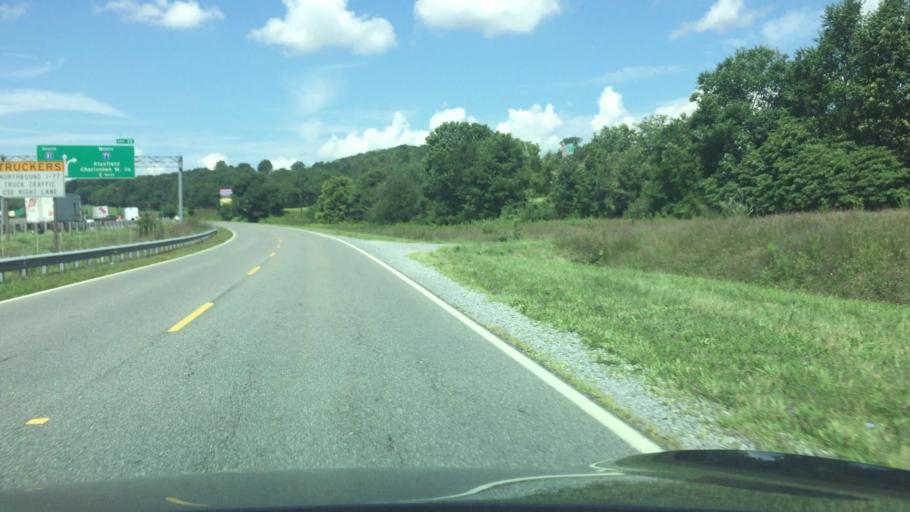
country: US
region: Virginia
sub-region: Wythe County
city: Wytheville
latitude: 36.9472
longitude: -81.0334
